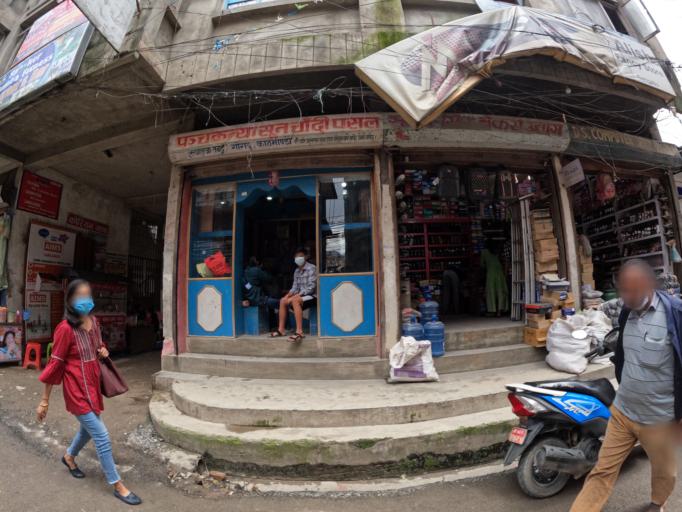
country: NP
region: Central Region
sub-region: Bagmati Zone
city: Kathmandu
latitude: 27.7359
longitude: 85.3145
